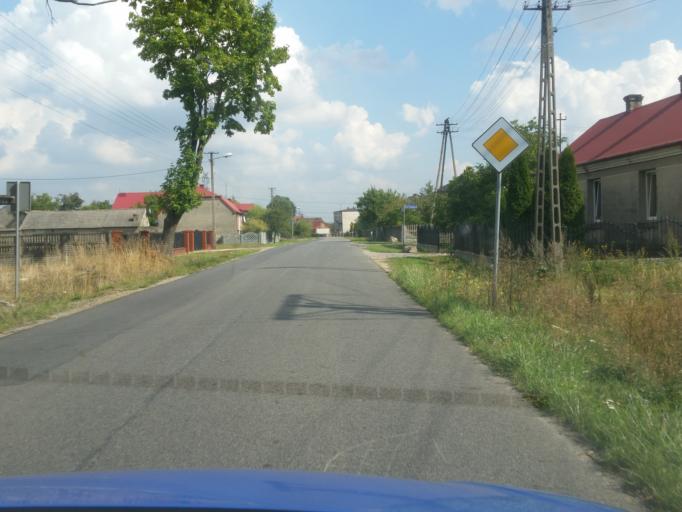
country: PL
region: Silesian Voivodeship
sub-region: Powiat czestochowski
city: Klomnice
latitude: 50.9645
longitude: 19.3364
